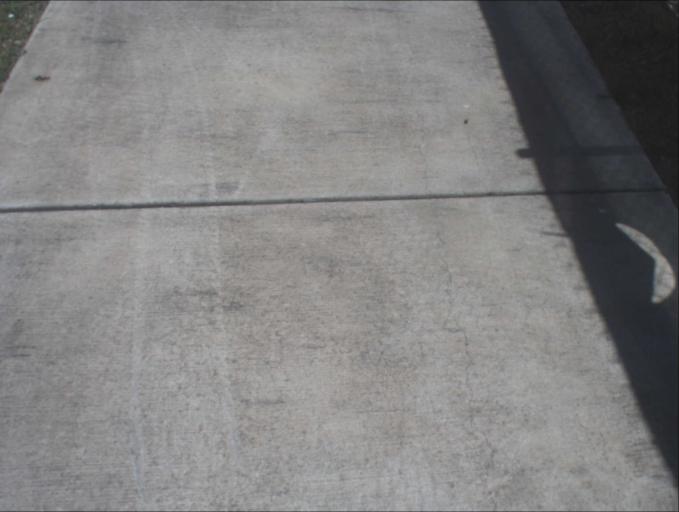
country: AU
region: Queensland
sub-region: Logan
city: Woodridge
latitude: -27.6461
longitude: 153.0949
